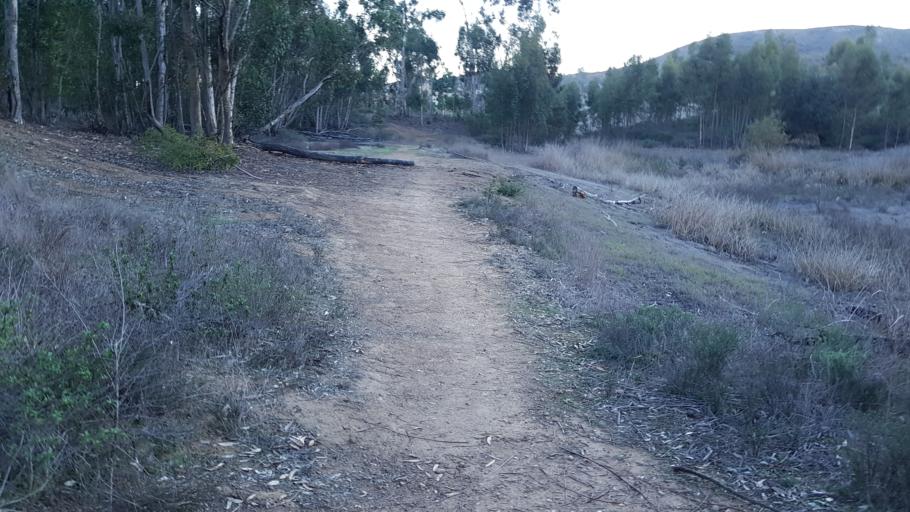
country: US
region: California
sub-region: San Diego County
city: Escondido
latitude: 33.0416
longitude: -117.1150
